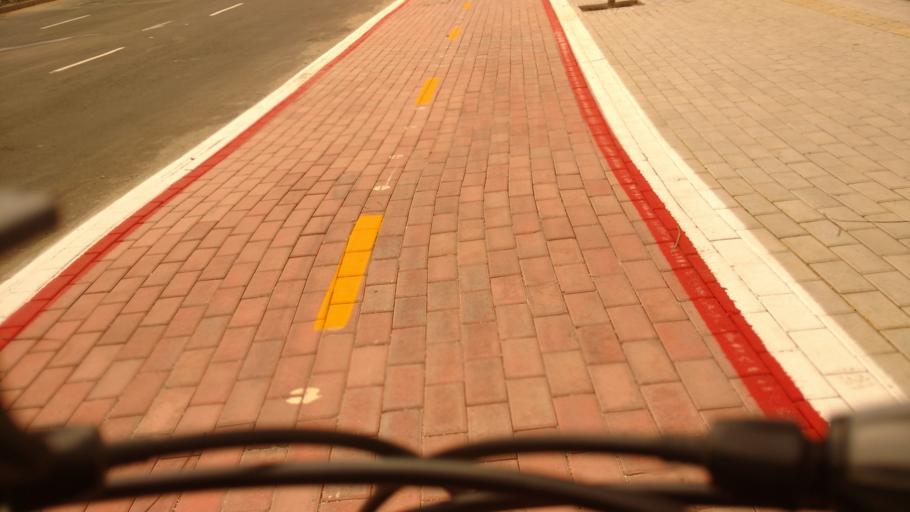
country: BR
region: Ceara
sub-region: Fortaleza
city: Fortaleza
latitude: -3.7440
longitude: -38.4874
